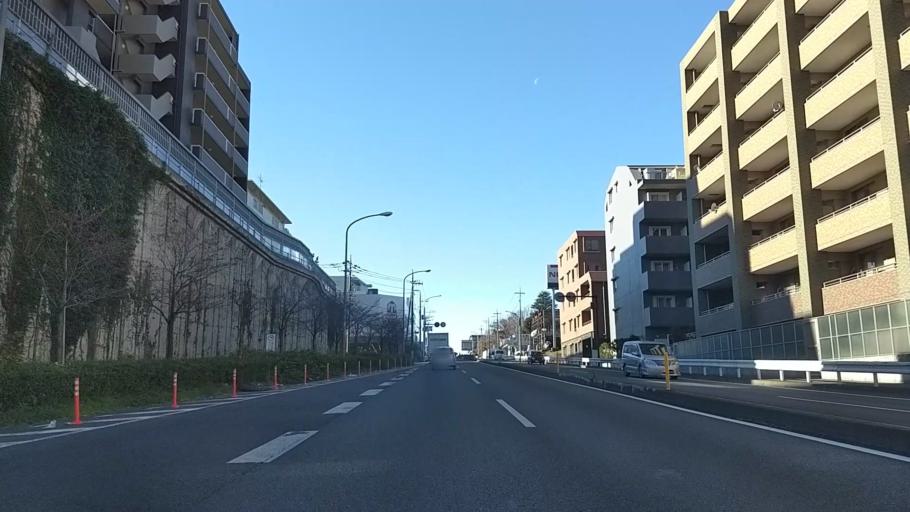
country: JP
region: Tokyo
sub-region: Machida-shi
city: Machida
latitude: 35.5482
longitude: 139.5325
